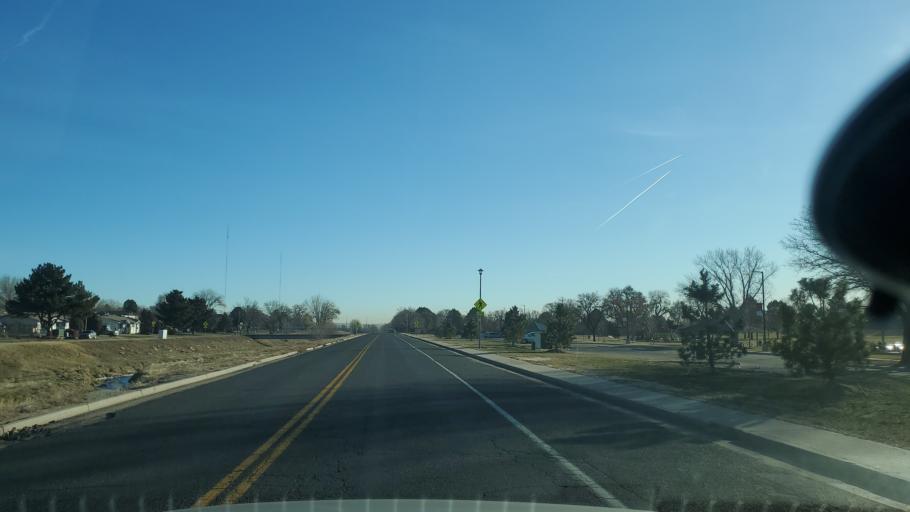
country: US
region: Colorado
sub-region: Adams County
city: Welby
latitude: 39.8419
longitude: -104.9668
